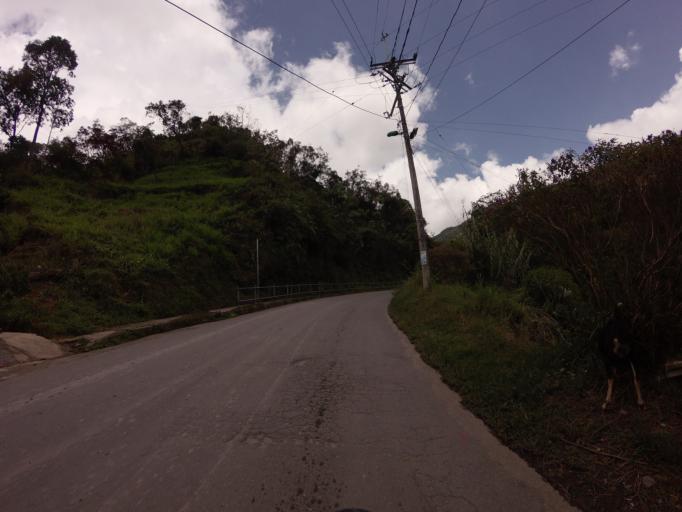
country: CO
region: Caldas
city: Manzanares
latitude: 5.2567
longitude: -75.1500
